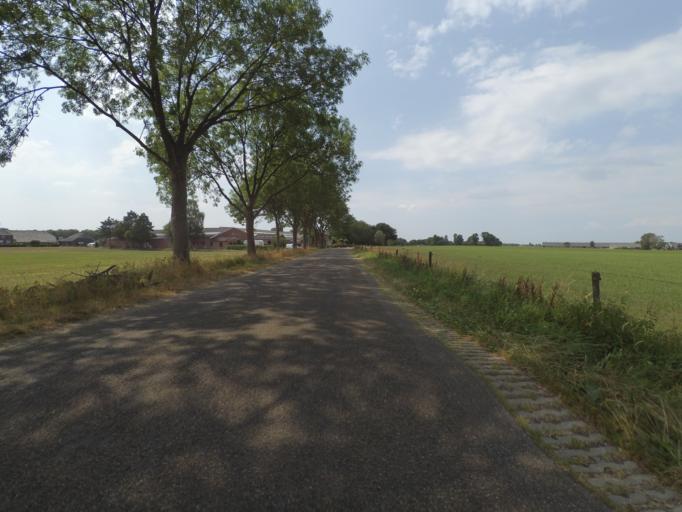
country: NL
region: Gelderland
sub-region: Oude IJsselstreek
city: Gendringen
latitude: 51.8706
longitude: 6.4244
